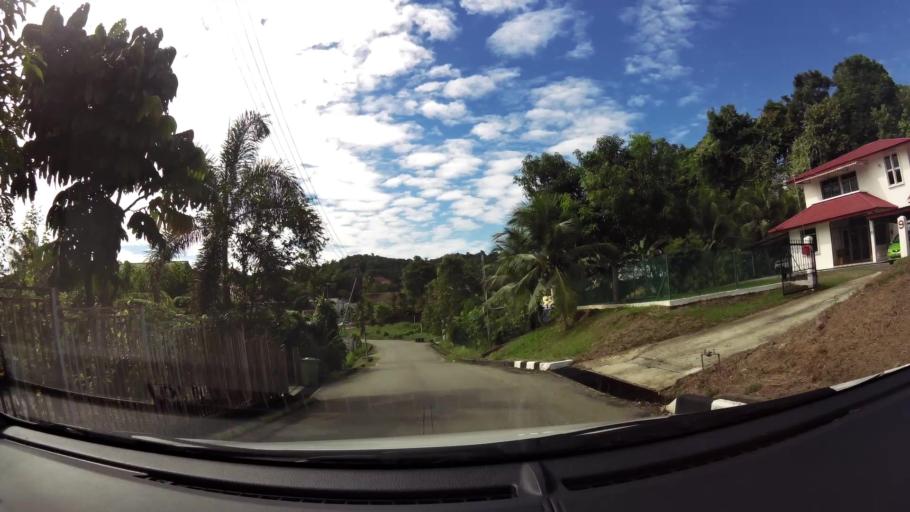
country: BN
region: Brunei and Muara
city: Bandar Seri Begawan
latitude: 4.9113
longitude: 114.9814
